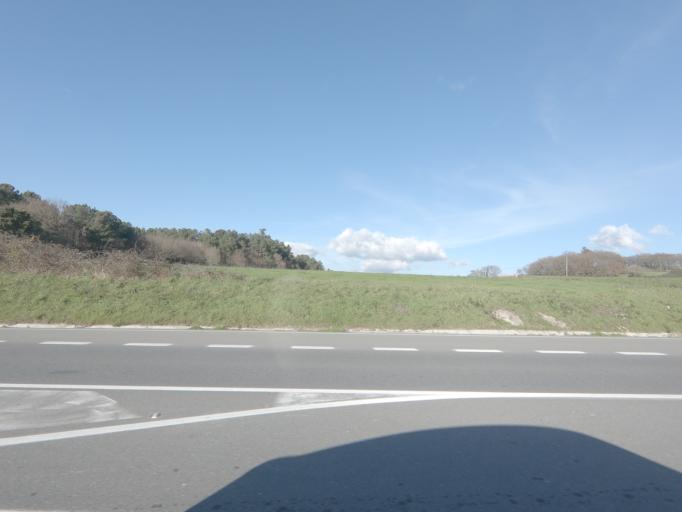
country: ES
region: Galicia
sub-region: Provincia de Pontevedra
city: Silleda
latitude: 42.7091
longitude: -8.2709
